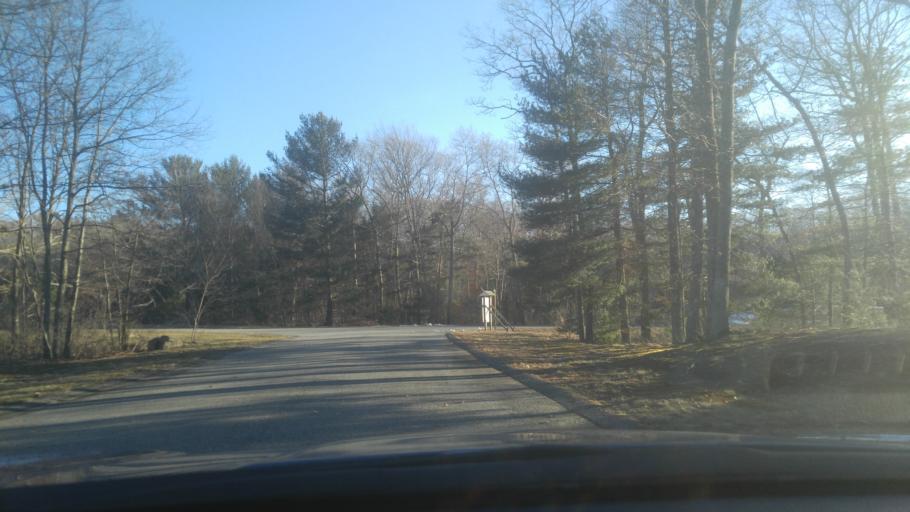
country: US
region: Rhode Island
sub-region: Kent County
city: West Warwick
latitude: 41.6475
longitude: -71.5551
